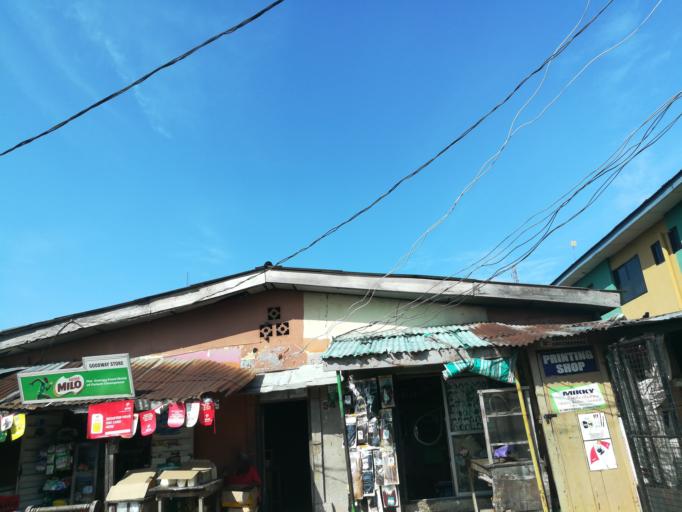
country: NG
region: Lagos
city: Ikeja
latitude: 6.6012
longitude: 3.3395
